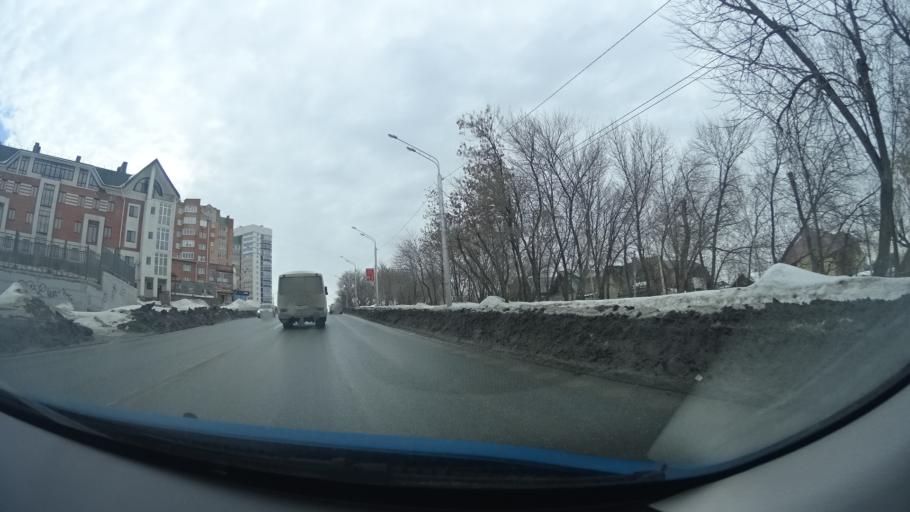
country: RU
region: Bashkortostan
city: Ufa
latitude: 54.7038
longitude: 55.9757
